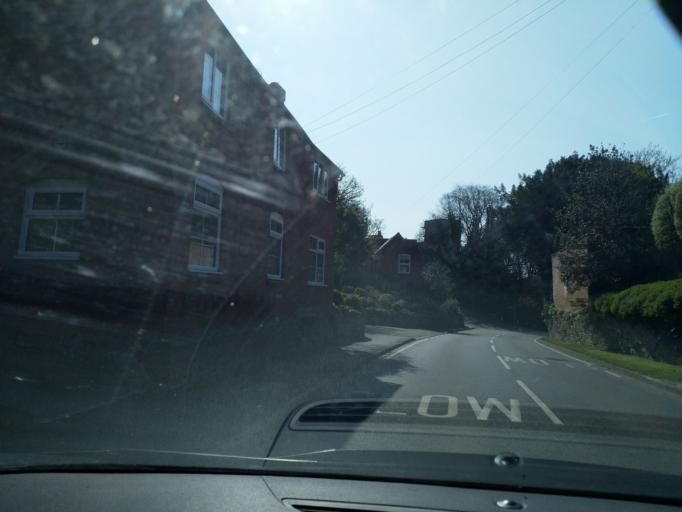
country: GB
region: England
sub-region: Warwickshire
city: Bidford-on-avon
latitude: 52.1848
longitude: -1.7895
